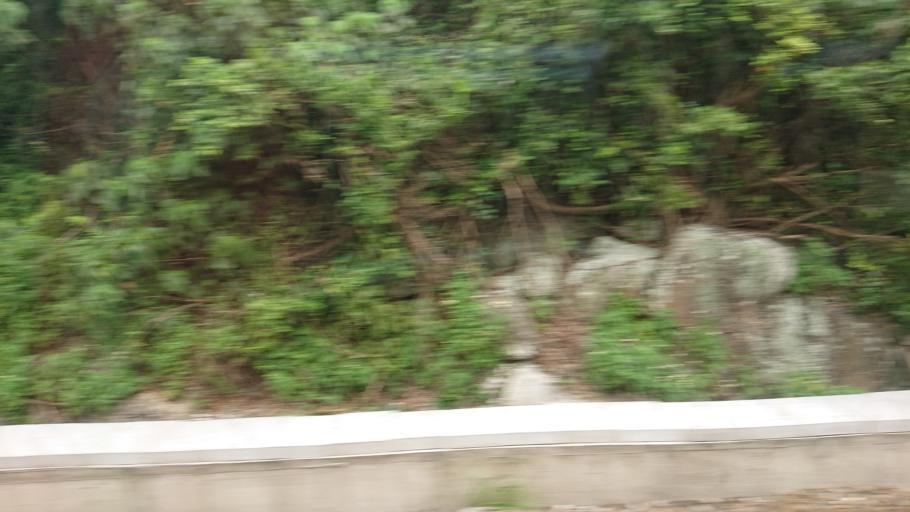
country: TW
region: Taiwan
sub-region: Yilan
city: Yilan
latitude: 24.9217
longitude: 121.8829
